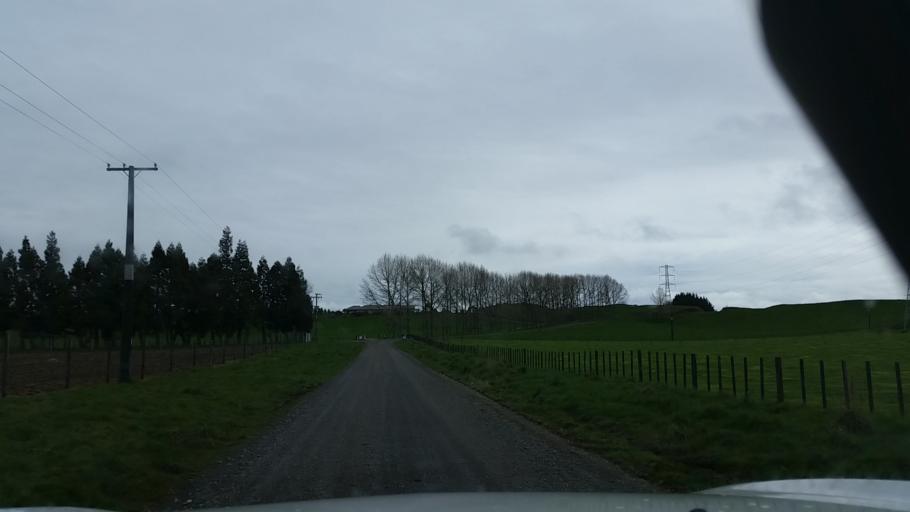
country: NZ
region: Bay of Plenty
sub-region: Rotorua District
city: Rotorua
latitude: -38.0088
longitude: 176.1961
